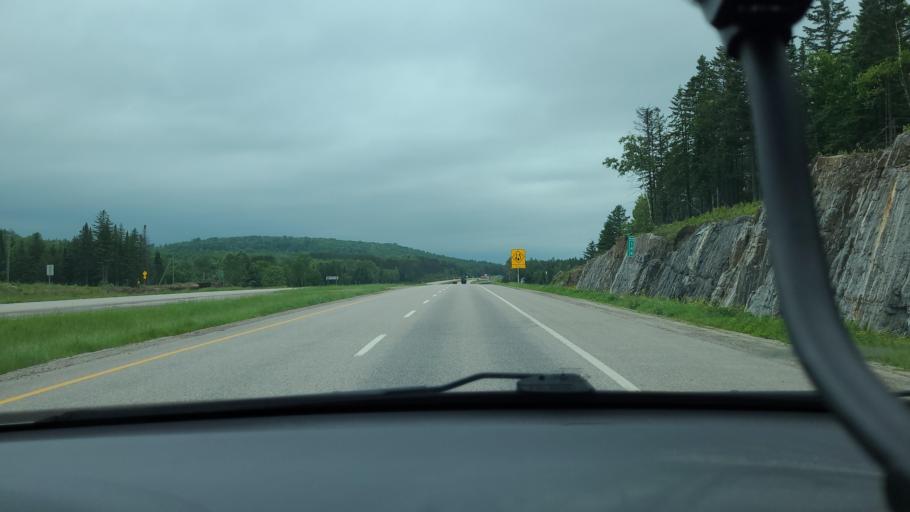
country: CA
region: Quebec
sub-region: Laurentides
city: Labelle
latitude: 46.2826
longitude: -74.7580
